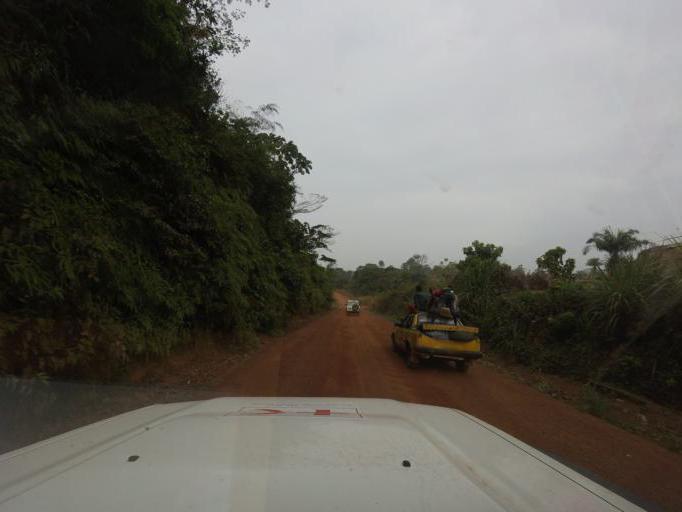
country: LR
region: Lofa
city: Voinjama
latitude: 8.3831
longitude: -9.8342
